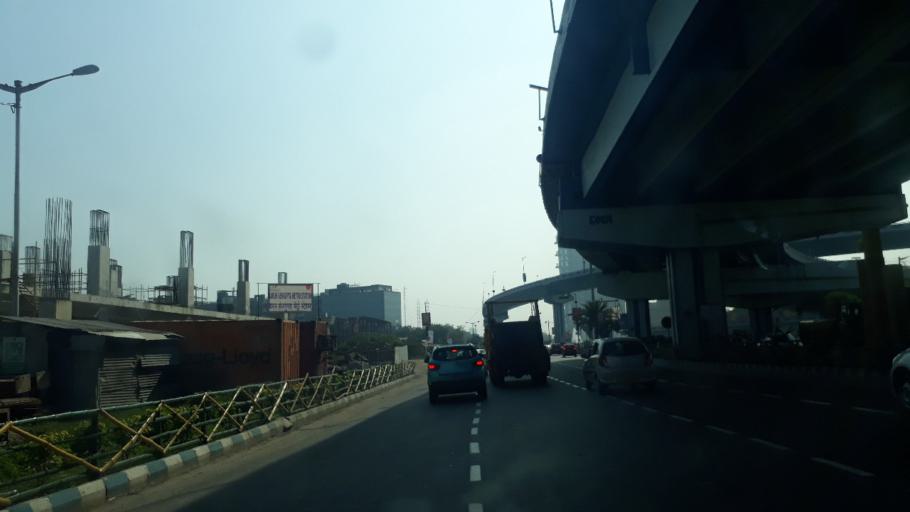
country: IN
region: West Bengal
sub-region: Kolkata
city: Kolkata
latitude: 22.5440
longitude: 88.3989
